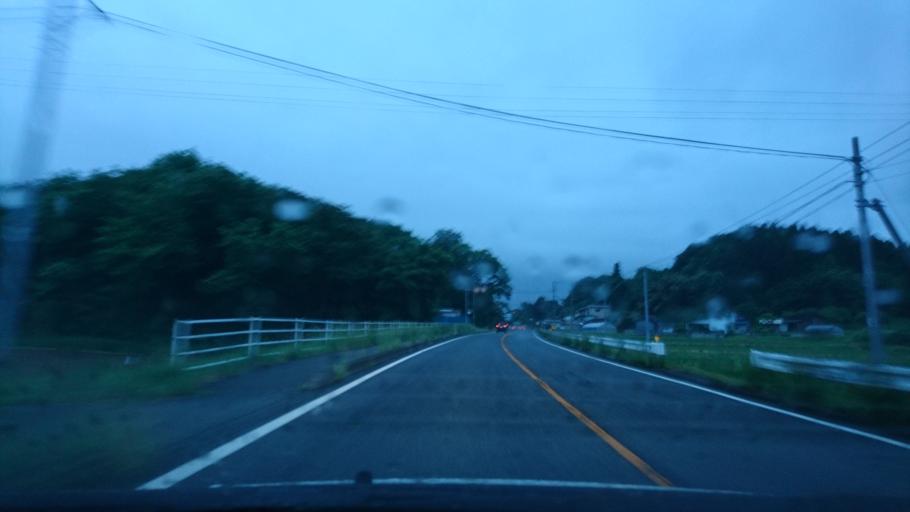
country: JP
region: Iwate
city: Ichinoseki
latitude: 38.7856
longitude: 141.0497
